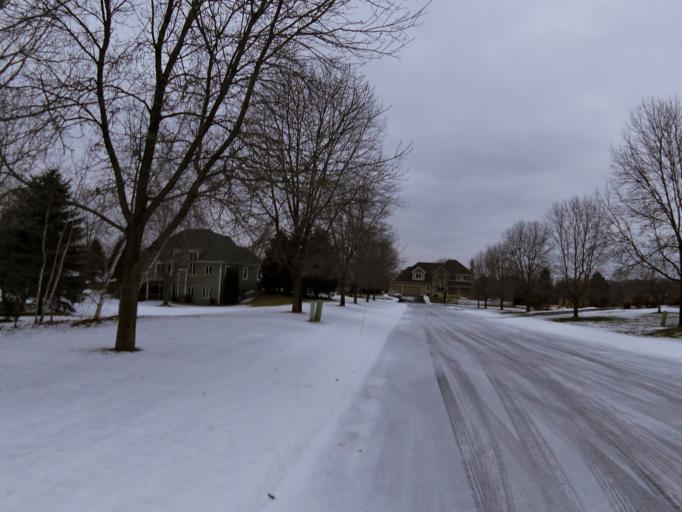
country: US
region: Minnesota
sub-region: Washington County
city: Lake Elmo
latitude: 44.9614
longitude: -92.8596
